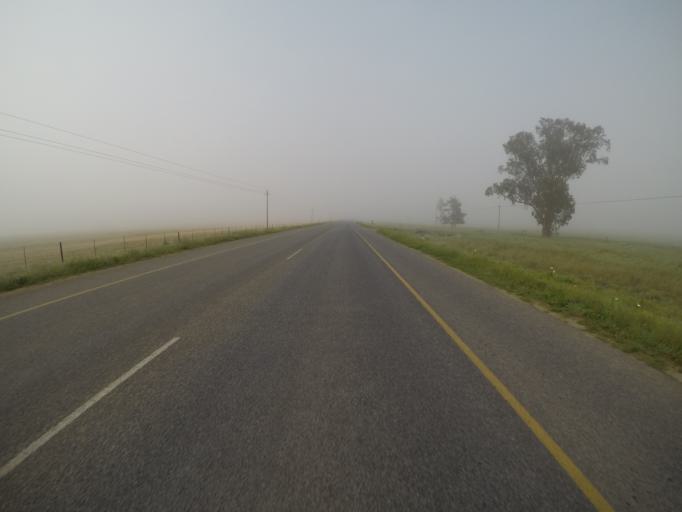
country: ZA
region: Western Cape
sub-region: City of Cape Town
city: Kraaifontein
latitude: -33.6730
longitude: 18.7070
